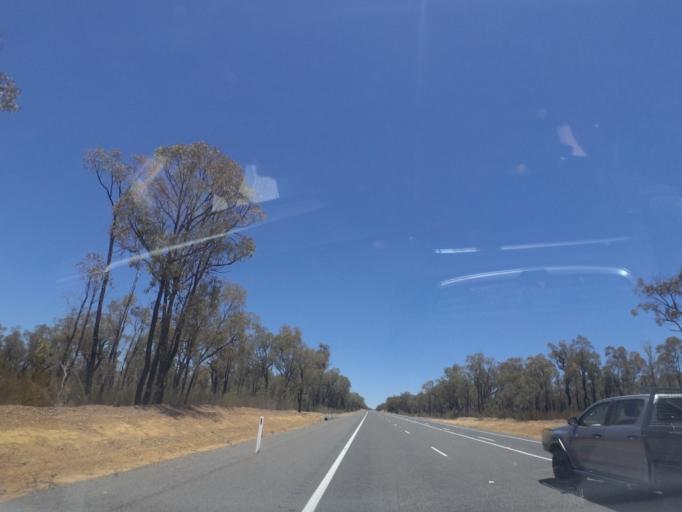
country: AU
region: New South Wales
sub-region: Warrumbungle Shire
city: Coonabarabran
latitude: -30.8967
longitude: 149.4406
